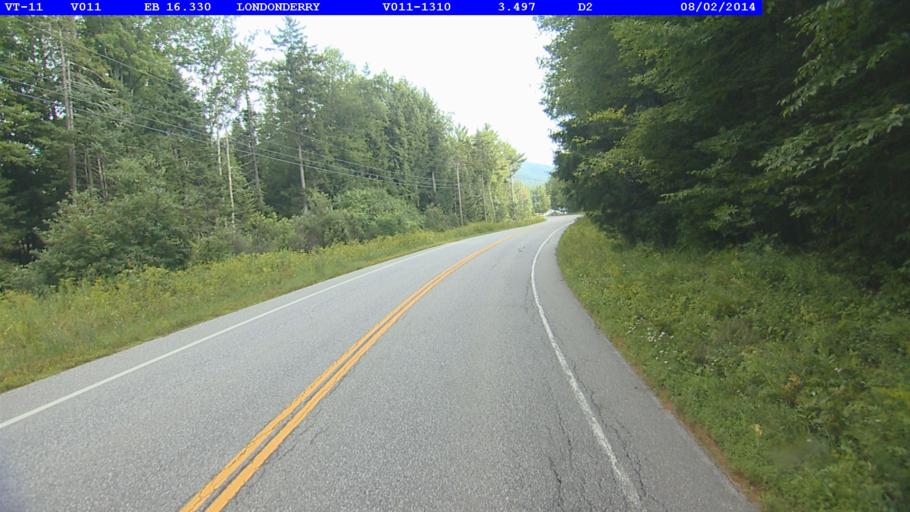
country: US
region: Vermont
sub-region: Windsor County
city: Chester
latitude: 43.2175
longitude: -72.7908
